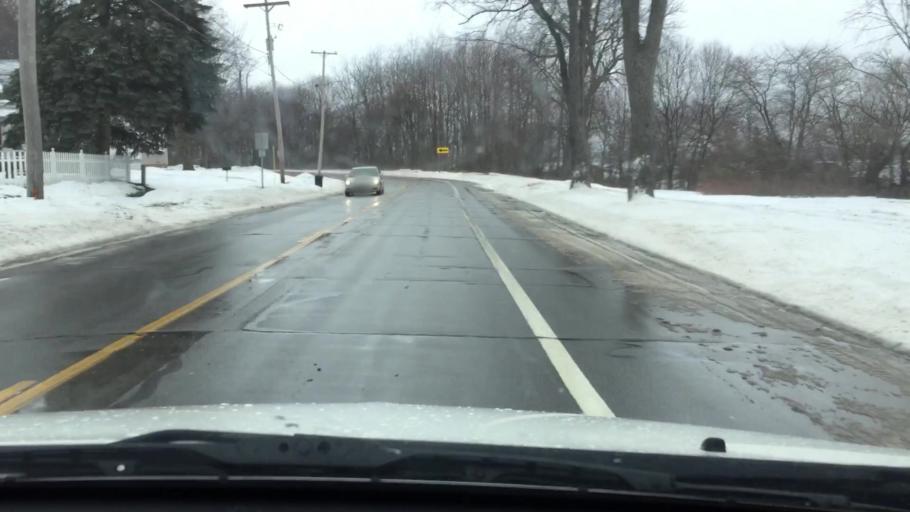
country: US
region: Michigan
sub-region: Wexford County
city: Cadillac
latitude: 44.2410
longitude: -85.4049
